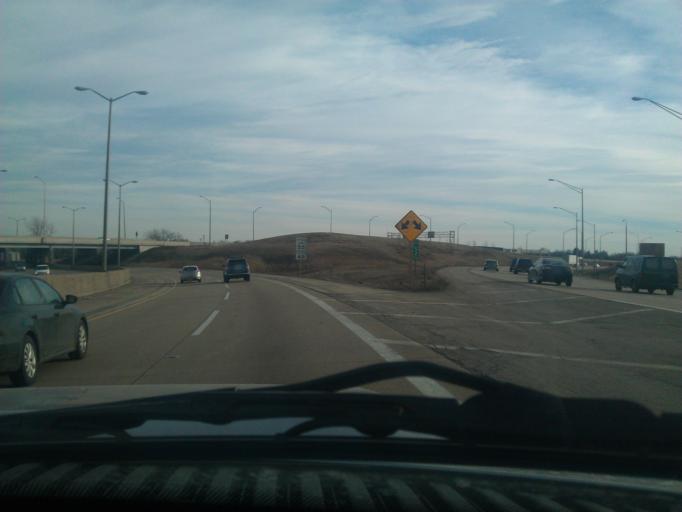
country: US
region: Illinois
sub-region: Lake County
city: Riverwoods
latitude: 42.1528
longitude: -87.8744
